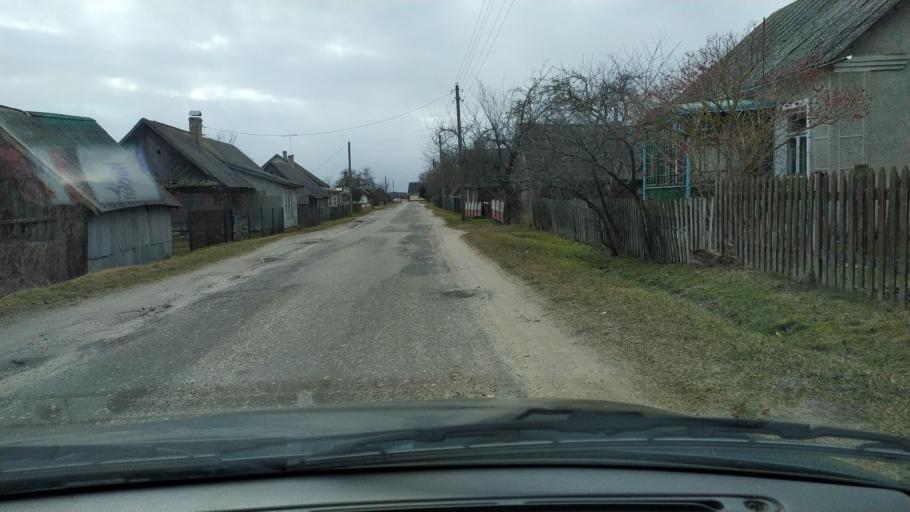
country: BY
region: Brest
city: Kamyanyets
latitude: 52.4039
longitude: 23.7955
